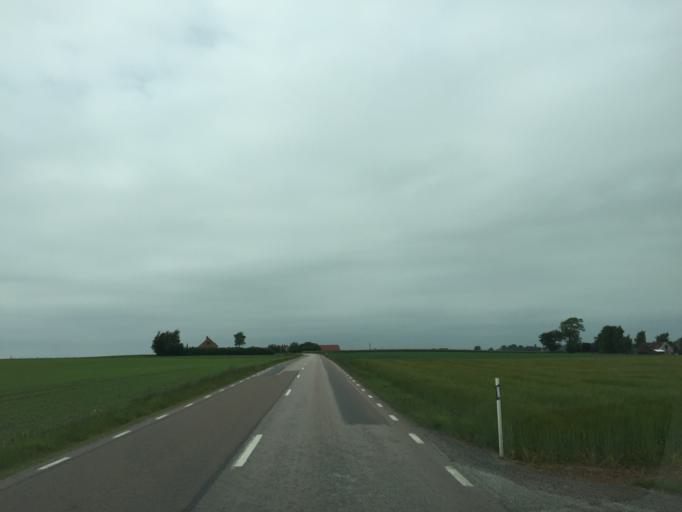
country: SE
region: Skane
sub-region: Ystads Kommun
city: Kopingebro
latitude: 55.4291
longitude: 14.0871
